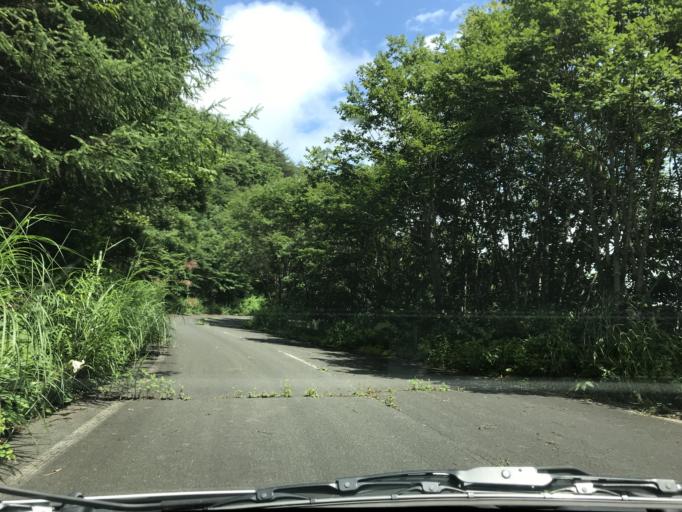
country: JP
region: Iwate
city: Tono
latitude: 39.0975
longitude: 141.4186
